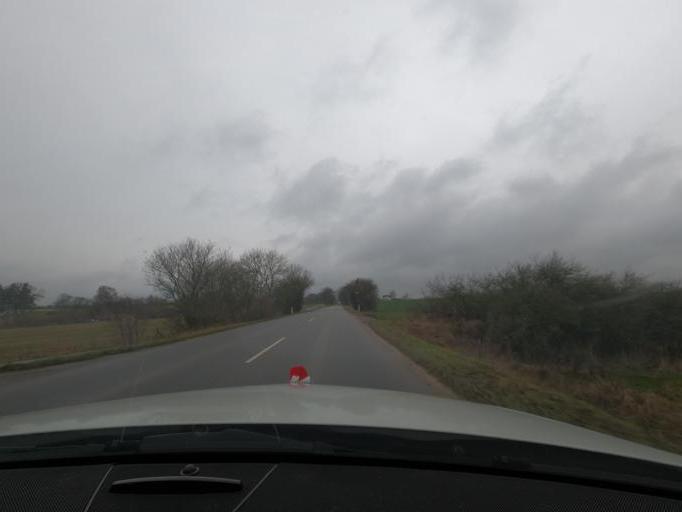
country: DK
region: South Denmark
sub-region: Haderslev Kommune
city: Starup
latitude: 55.1926
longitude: 9.5706
